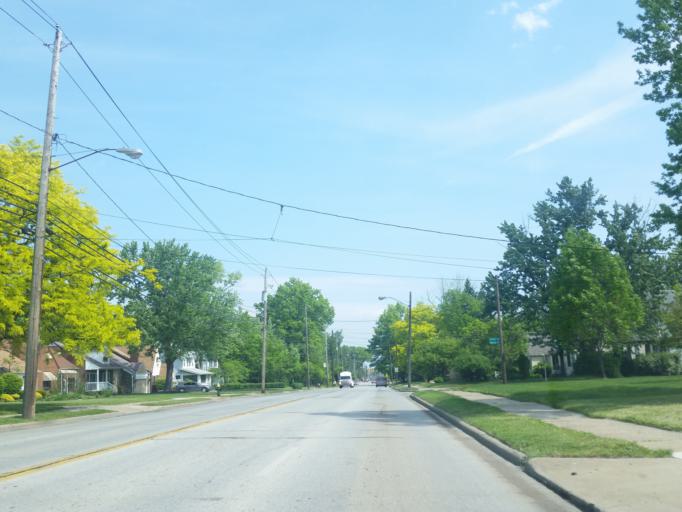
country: US
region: Ohio
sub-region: Cuyahoga County
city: South Euclid
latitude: 41.5130
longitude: -81.5194
